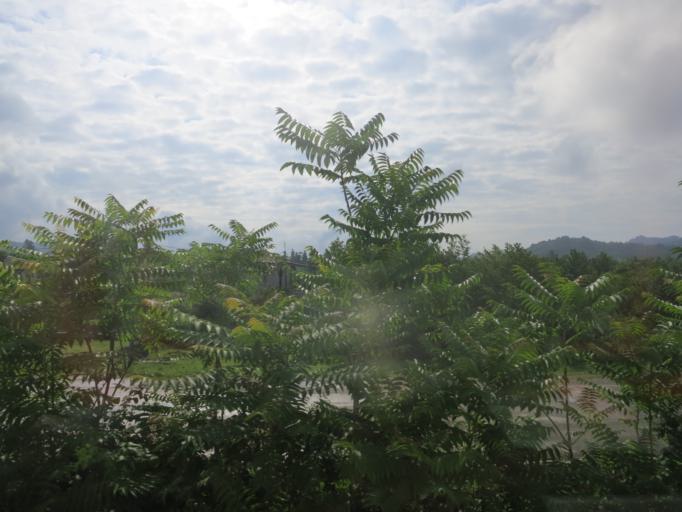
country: GE
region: Guria
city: Urek'i
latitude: 42.0343
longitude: 41.8122
